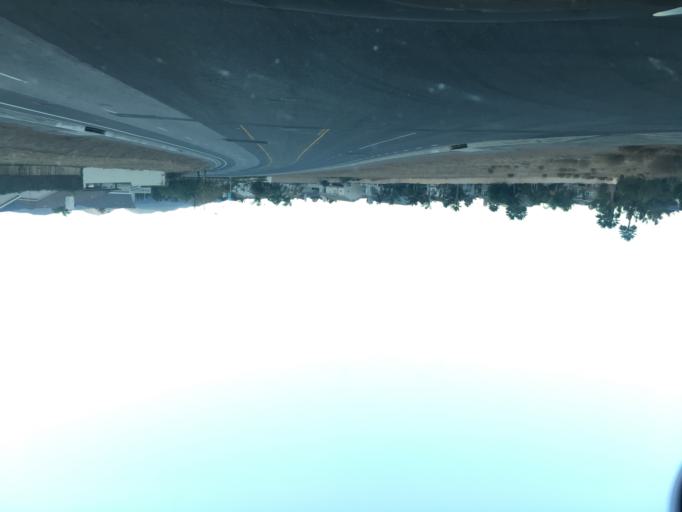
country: US
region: California
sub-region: Riverside County
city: El Cerrito
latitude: 33.8480
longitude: -117.5525
